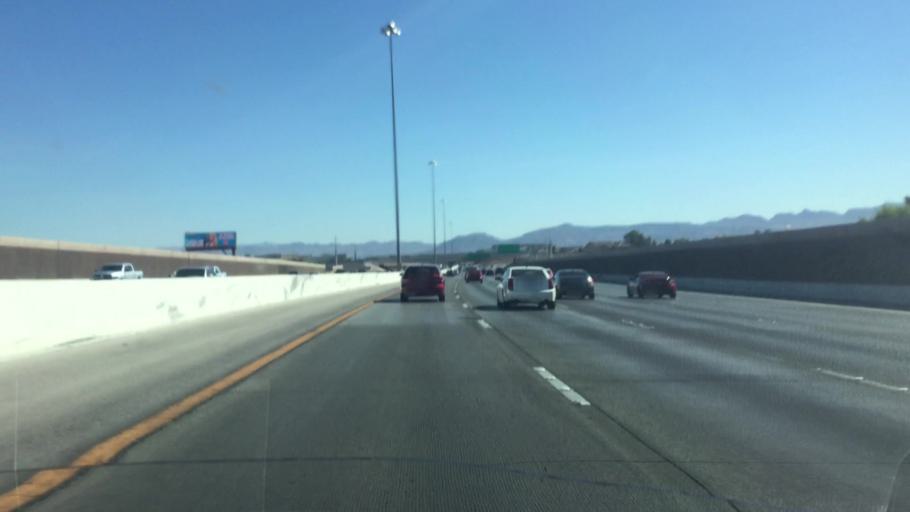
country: US
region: Nevada
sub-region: Clark County
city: Paradise
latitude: 36.0680
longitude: -115.1955
